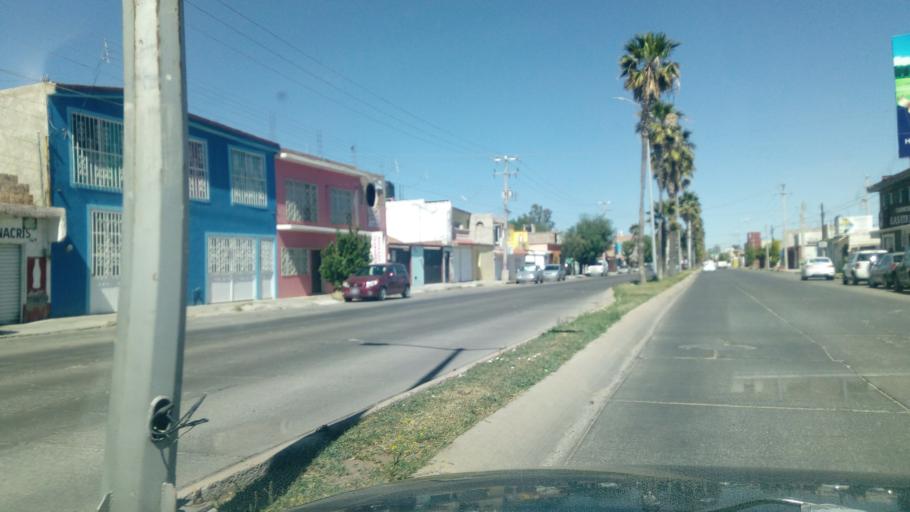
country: MX
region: Durango
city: Victoria de Durango
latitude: 24.0111
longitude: -104.6881
